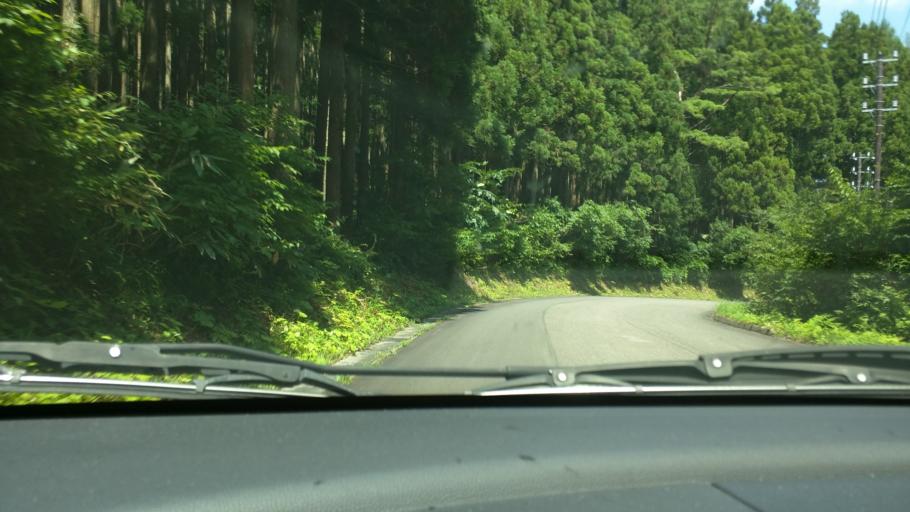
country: JP
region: Fukushima
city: Inawashiro
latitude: 37.3582
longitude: 140.0572
